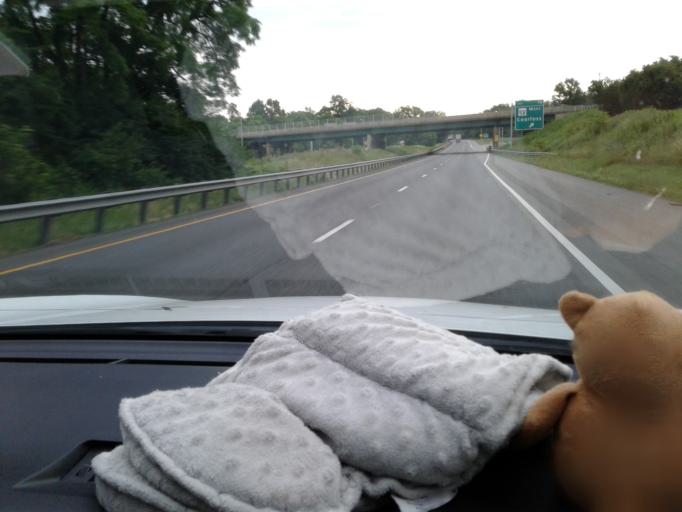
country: US
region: Maryland
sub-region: Washington County
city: Hagerstown
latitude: 39.6621
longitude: -77.7410
